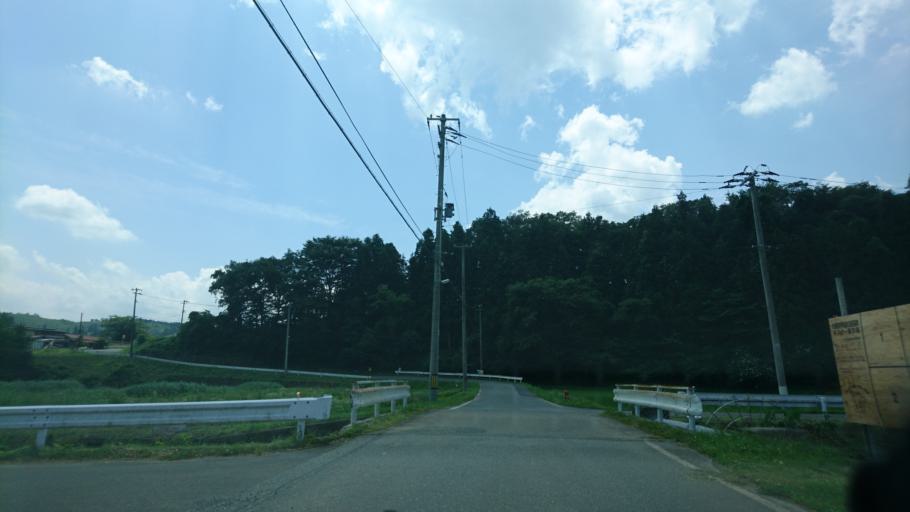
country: JP
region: Iwate
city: Ichinoseki
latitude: 38.9102
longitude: 141.2239
